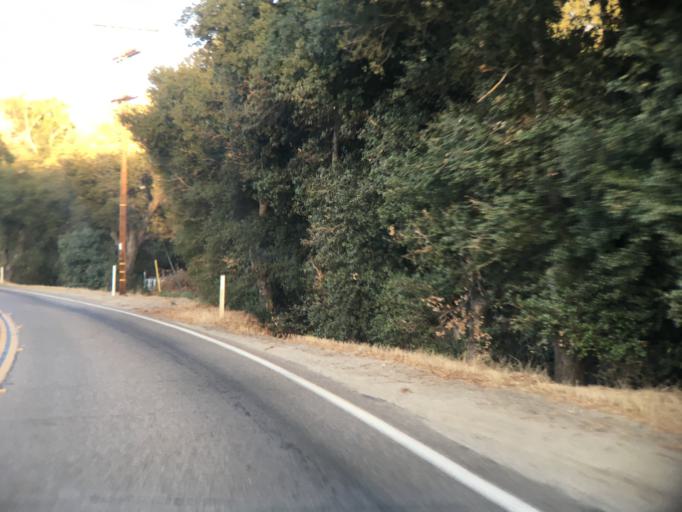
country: US
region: California
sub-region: San Diego County
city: Harbison Canyon
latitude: 32.8018
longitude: -116.8226
